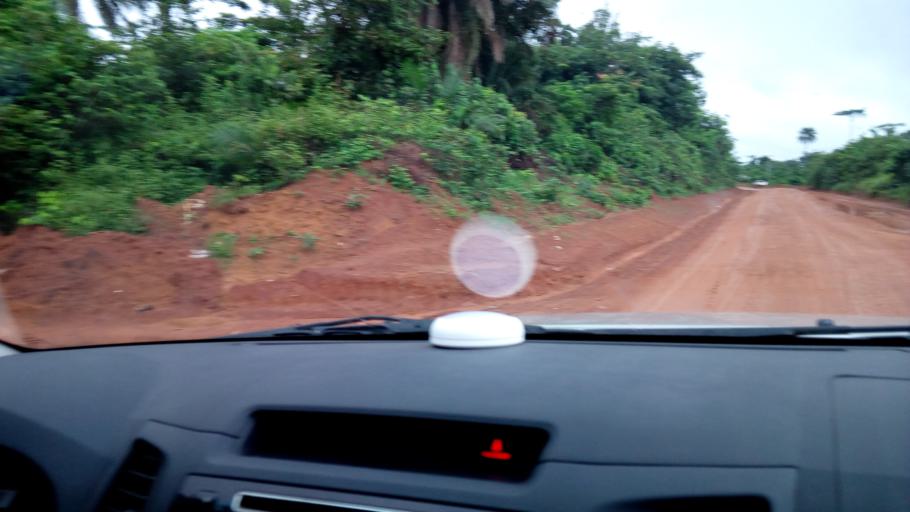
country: LR
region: Nimba
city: Sanniquellie
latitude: 7.1827
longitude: -8.9687
